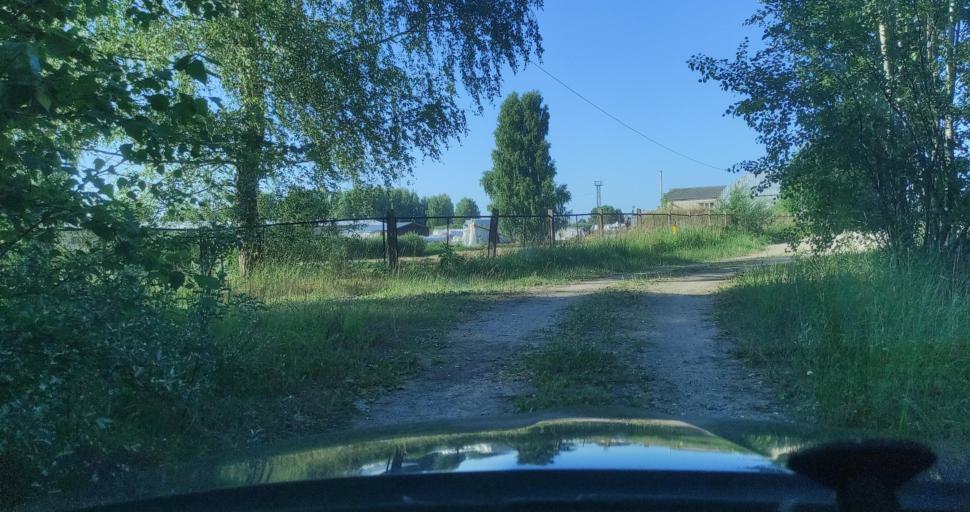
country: LV
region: Skrunda
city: Skrunda
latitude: 56.6827
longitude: 22.0043
